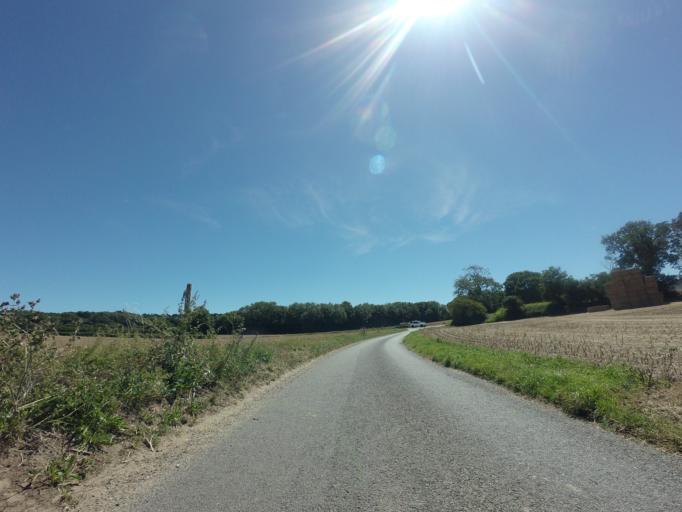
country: GB
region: England
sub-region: Kent
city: Deal
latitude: 51.1915
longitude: 1.3665
